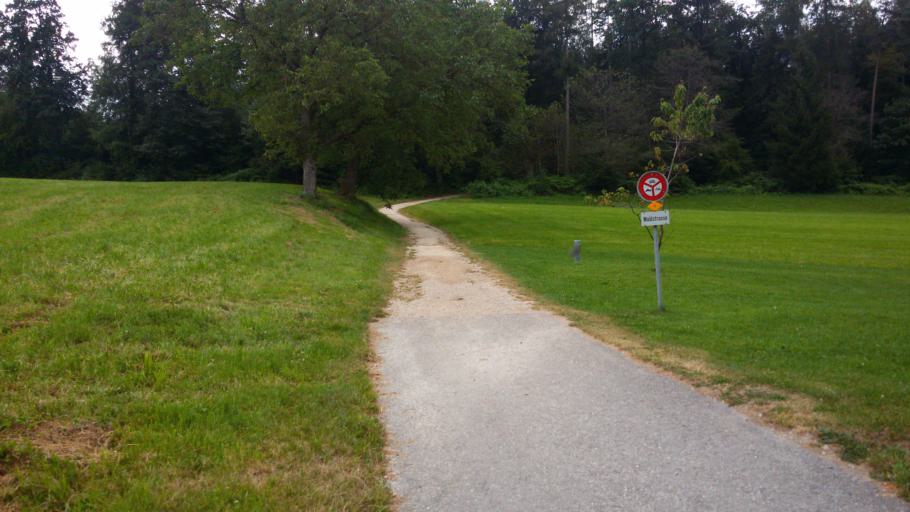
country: CH
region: Aargau
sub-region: Bezirk Baden
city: Untersiggenthal
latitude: 47.5123
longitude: 8.2685
